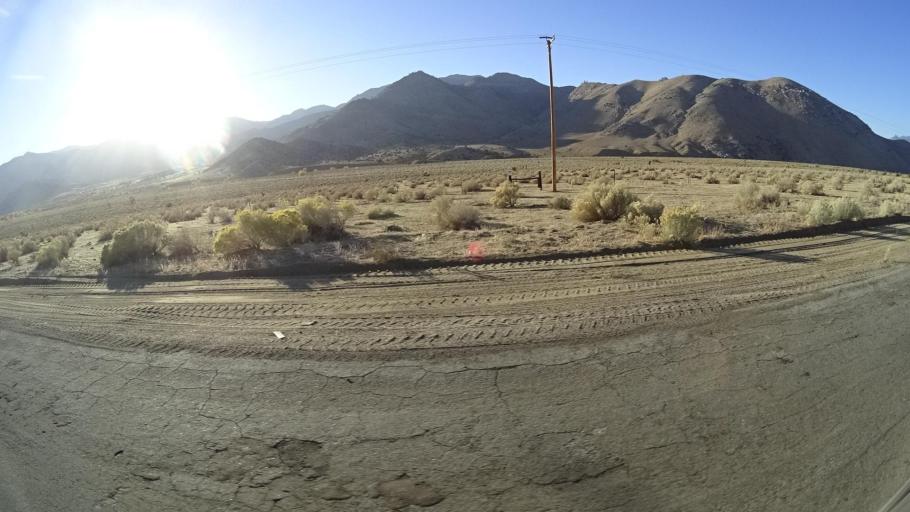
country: US
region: California
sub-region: Kern County
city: Weldon
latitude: 35.5943
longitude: -118.2400
